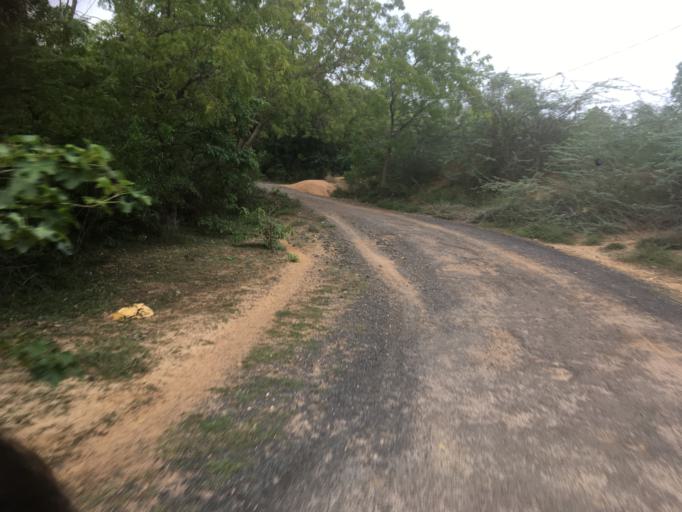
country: IN
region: Tamil Nadu
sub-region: Villupuram
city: Auroville
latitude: 12.0124
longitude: 79.8048
